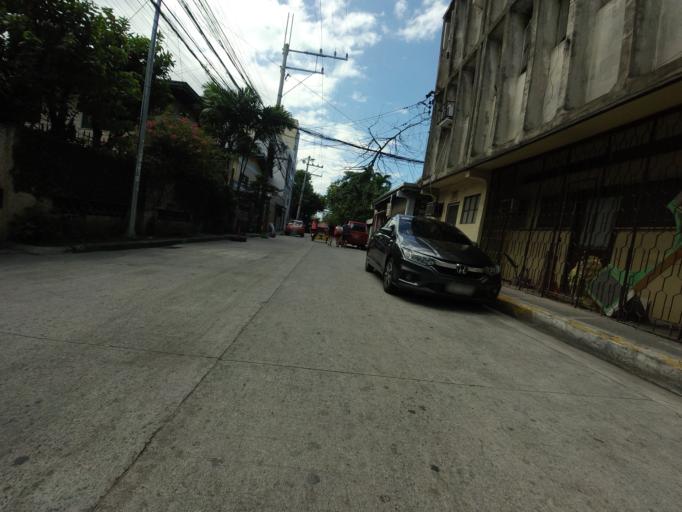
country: PH
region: Metro Manila
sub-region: San Juan
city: San Juan
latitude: 14.5803
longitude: 121.0112
